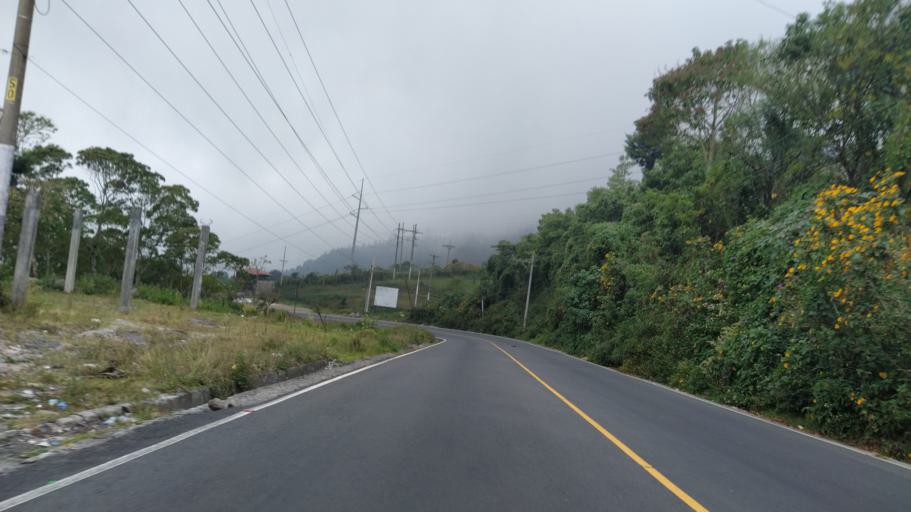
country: GT
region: Quetzaltenango
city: Zunil
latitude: 14.7340
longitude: -91.5234
